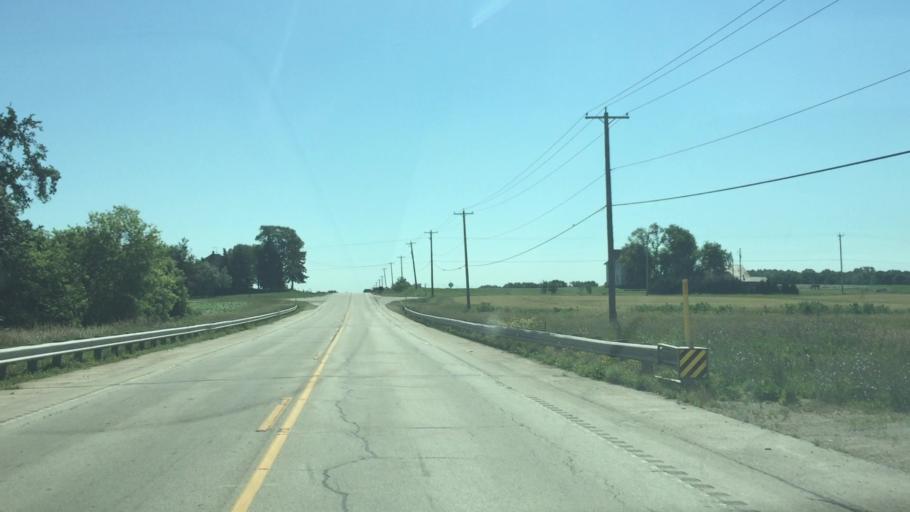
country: US
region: Wisconsin
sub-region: Calumet County
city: Hilbert
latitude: 44.1402
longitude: -88.1865
